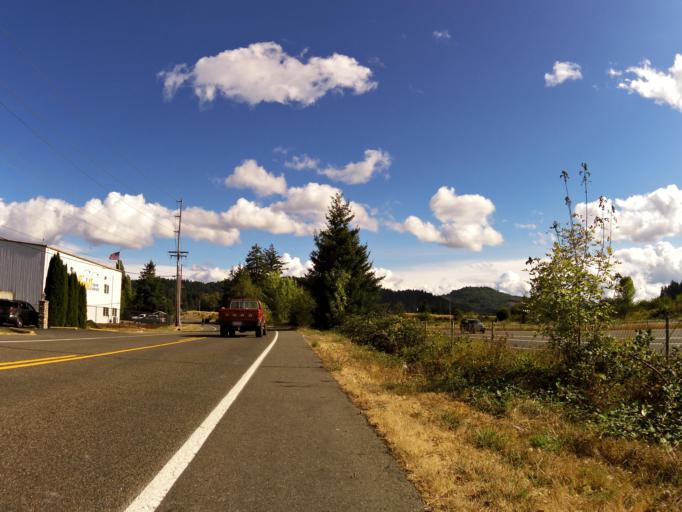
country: US
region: Washington
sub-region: Thurston County
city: Olympia
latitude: 47.0493
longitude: -122.9973
